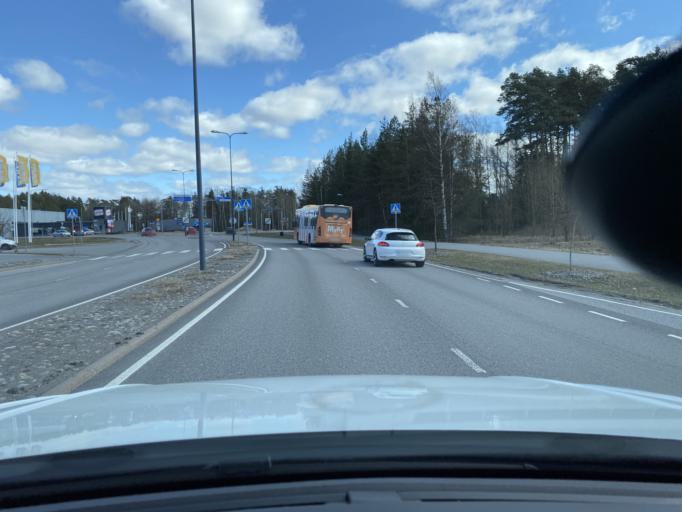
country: FI
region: Varsinais-Suomi
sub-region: Turku
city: Rusko
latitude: 60.4931
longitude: 22.2284
